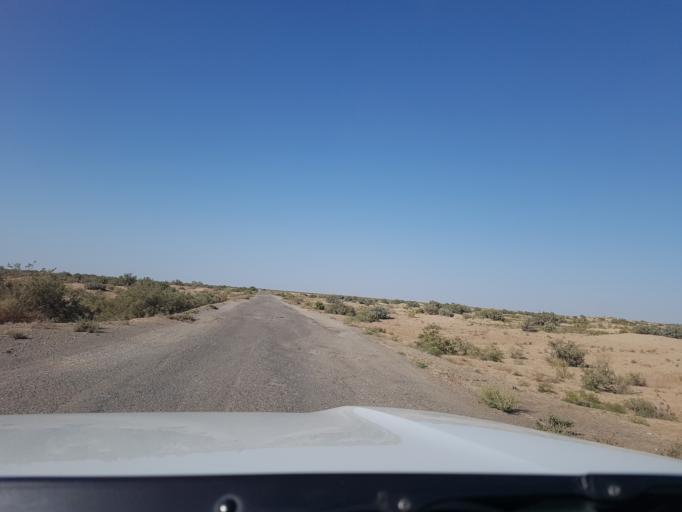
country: IR
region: Razavi Khorasan
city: Sarakhs
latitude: 36.8100
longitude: 61.3241
